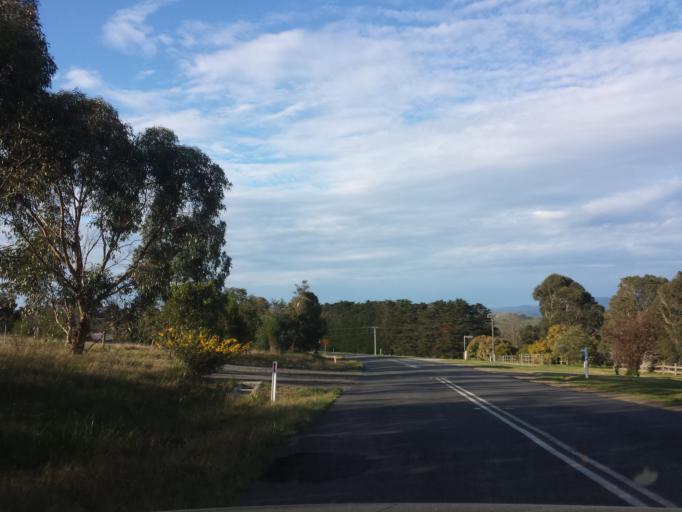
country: AU
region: Victoria
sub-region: Yarra Ranges
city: Yarra Glen
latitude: -37.6421
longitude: 145.3731
